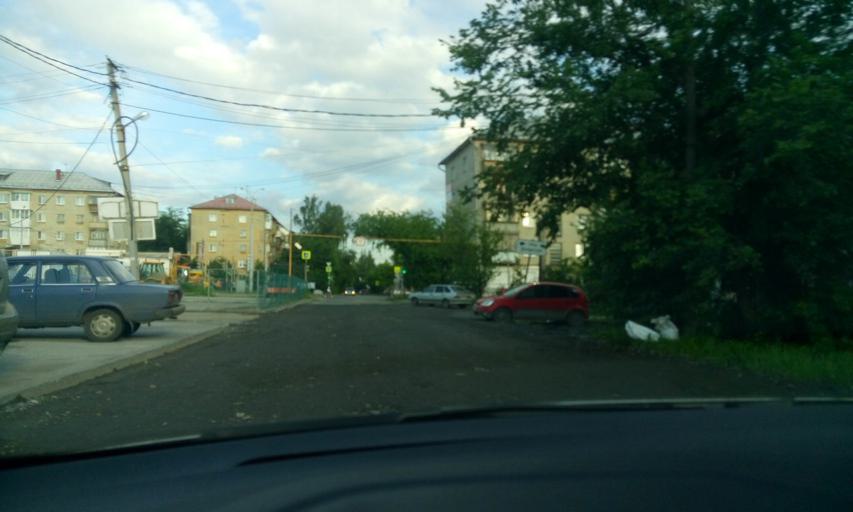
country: RU
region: Sverdlovsk
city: Yekaterinburg
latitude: 56.8883
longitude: 60.5652
